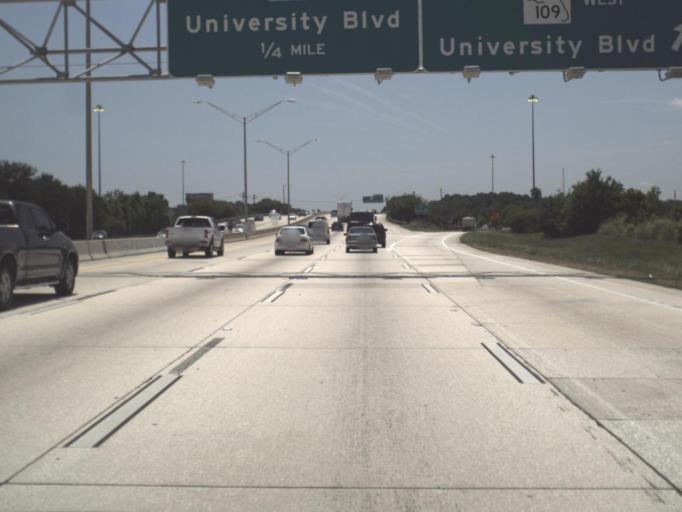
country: US
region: Florida
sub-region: Duval County
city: Jacksonville
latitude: 30.2723
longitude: -81.6143
